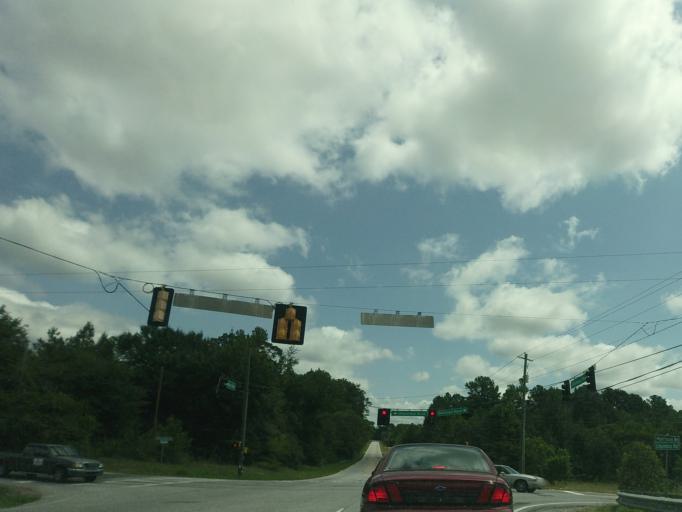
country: US
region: Georgia
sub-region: Bibb County
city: West Point
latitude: 32.8190
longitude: -83.7270
